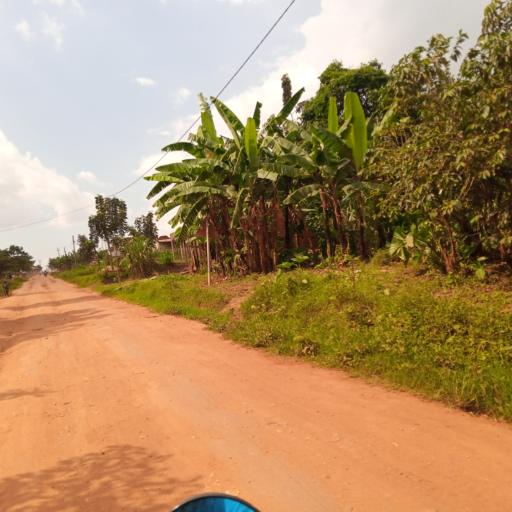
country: UG
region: Eastern Region
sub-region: Mbale District
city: Mbale
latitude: 1.1140
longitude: 34.2027
